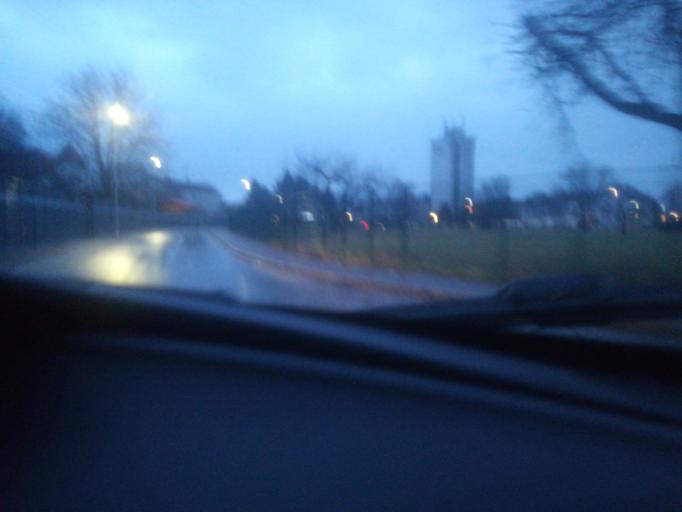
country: AT
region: Upper Austria
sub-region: Politischer Bezirk Perg
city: Perg
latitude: 48.2483
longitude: 14.6293
